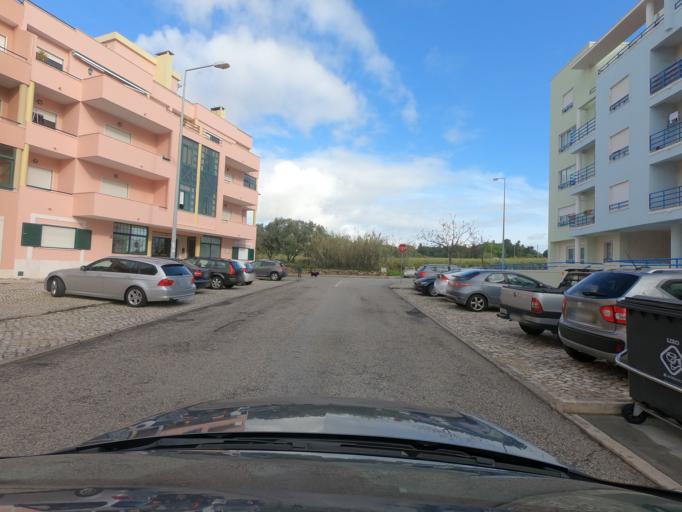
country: PT
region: Lisbon
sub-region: Cascais
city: Sao Domingos de Rana
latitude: 38.7010
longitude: -9.3225
